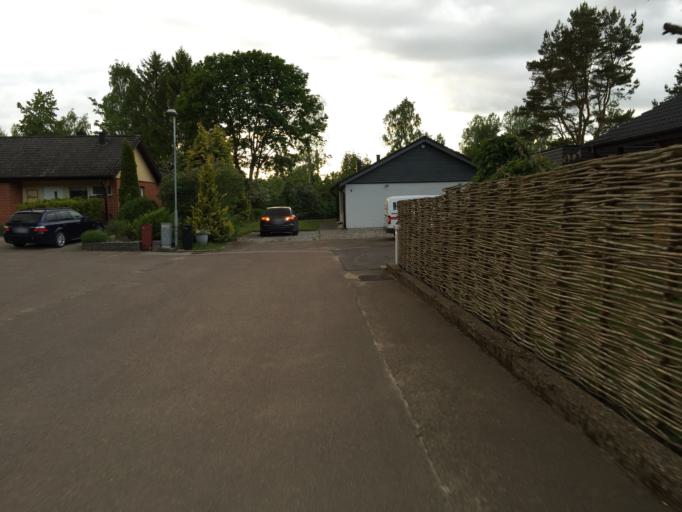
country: SE
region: Skane
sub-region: Lunds Kommun
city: Veberod
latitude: 55.6370
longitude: 13.5092
